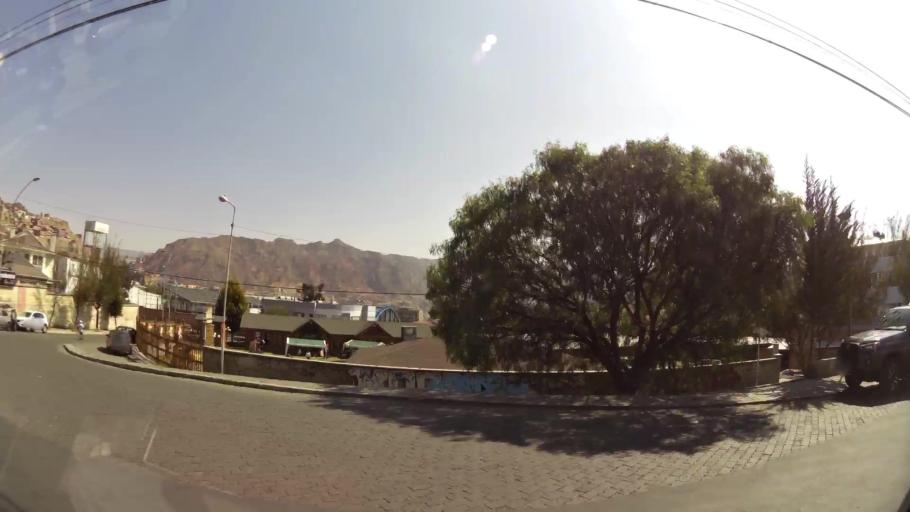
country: BO
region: La Paz
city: La Paz
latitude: -16.5434
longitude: -68.0810
